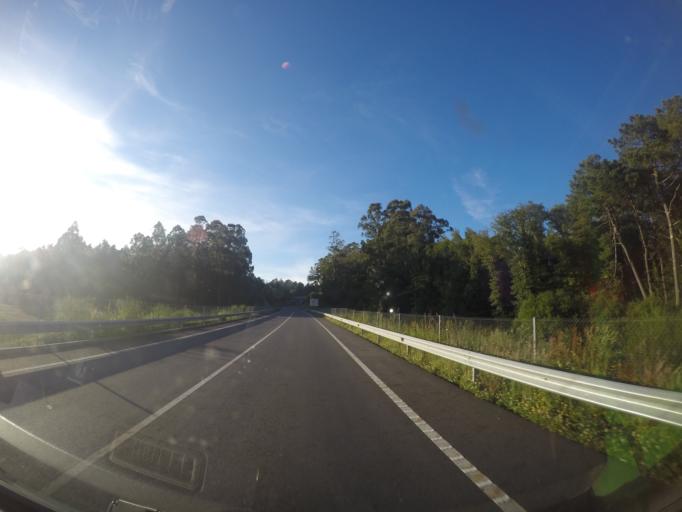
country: ES
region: Galicia
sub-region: Provincia da Coruna
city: Noia
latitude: 42.8065
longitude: -8.8890
